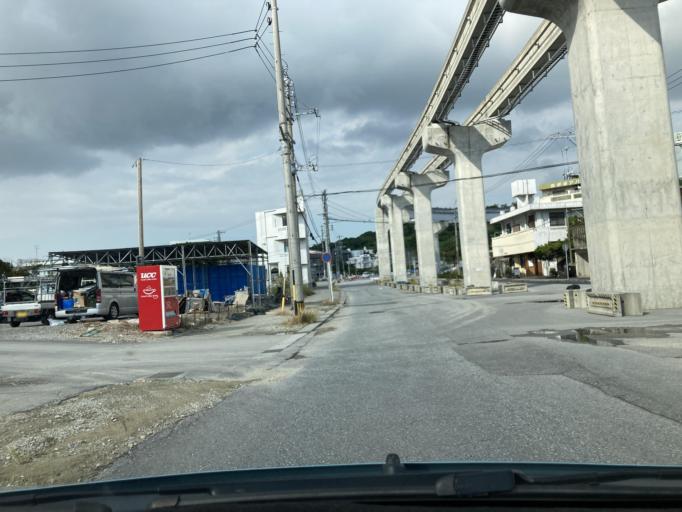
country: JP
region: Okinawa
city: Ginowan
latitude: 26.2421
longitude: 127.7308
